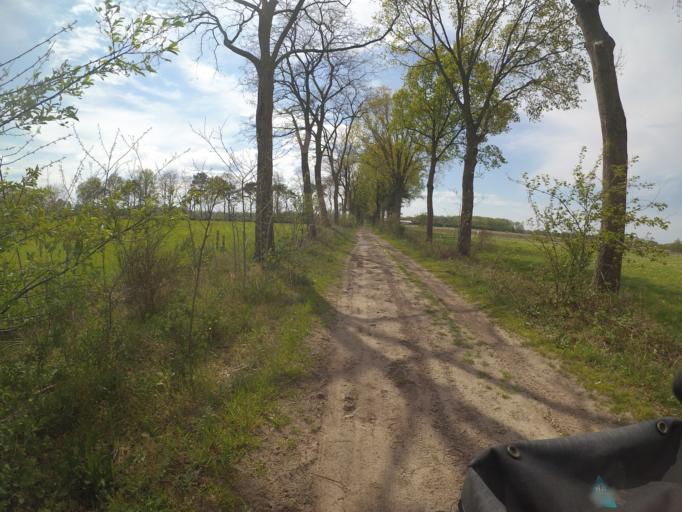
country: NL
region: North Brabant
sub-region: Gemeente Sint-Oedenrode
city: Sint-Oedenrode
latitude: 51.5874
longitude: 5.4749
